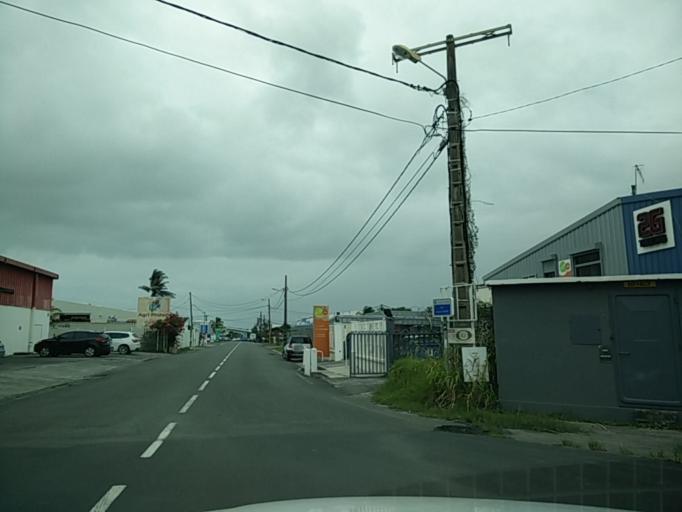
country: GP
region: Guadeloupe
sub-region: Guadeloupe
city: Pointe-a-Pitre
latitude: 16.2457
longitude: -61.5574
